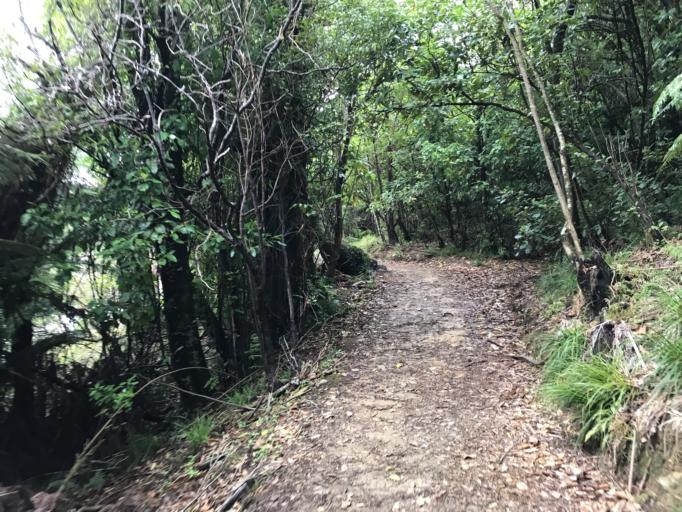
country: NZ
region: Marlborough
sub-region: Marlborough District
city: Picton
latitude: -41.1090
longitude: 174.1454
